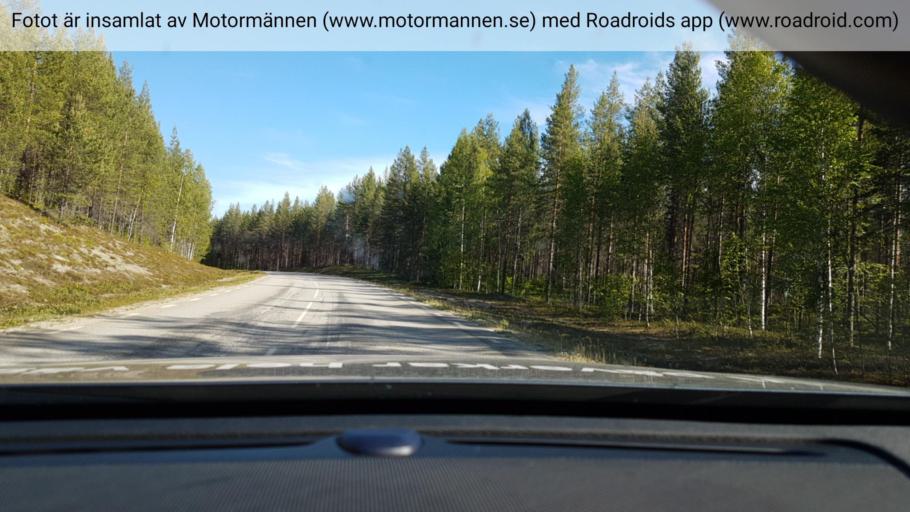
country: SE
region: Vaesterbotten
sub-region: Lycksele Kommun
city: Lycksele
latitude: 64.7984
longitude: 18.9564
